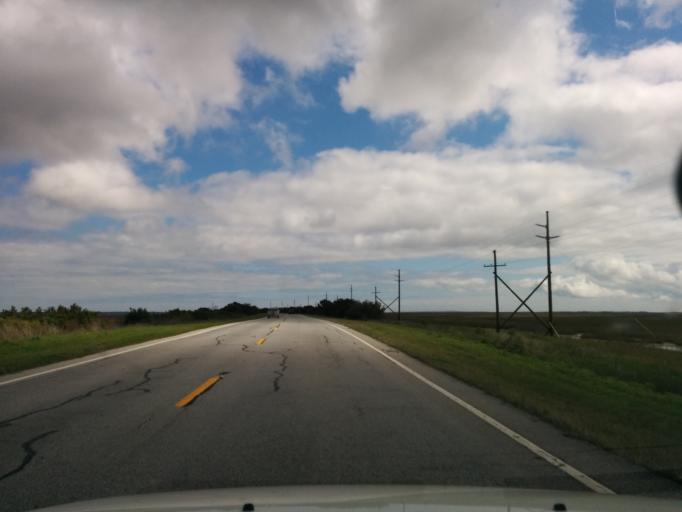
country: US
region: Georgia
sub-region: Glynn County
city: Brunswick
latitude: 31.0800
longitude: -81.4728
